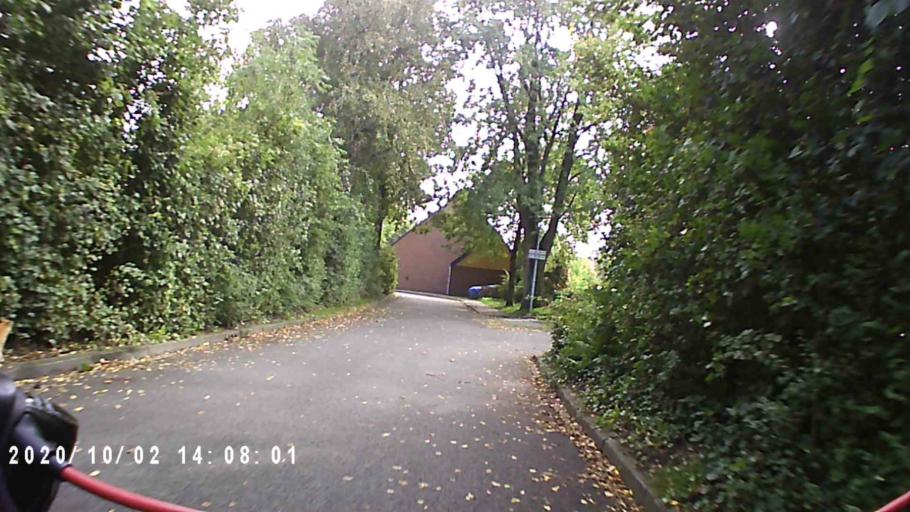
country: NL
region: Groningen
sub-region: Gemeente Zuidhorn
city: Zuidhorn
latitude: 53.2481
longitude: 6.3996
